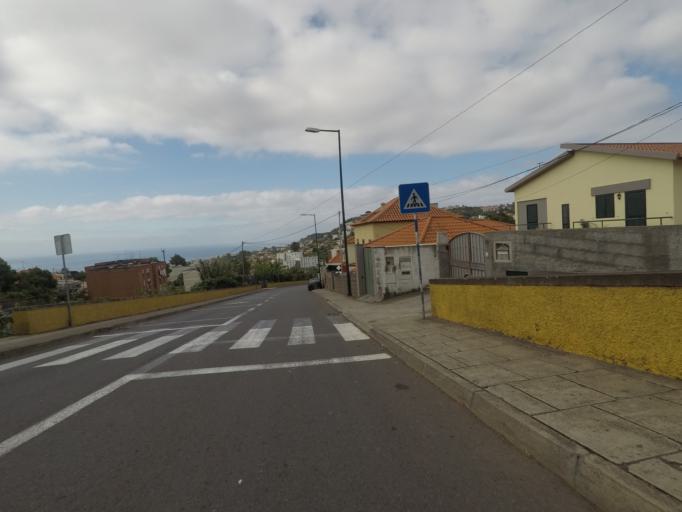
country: PT
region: Madeira
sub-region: Funchal
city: Nossa Senhora do Monte
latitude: 32.6690
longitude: -16.9368
